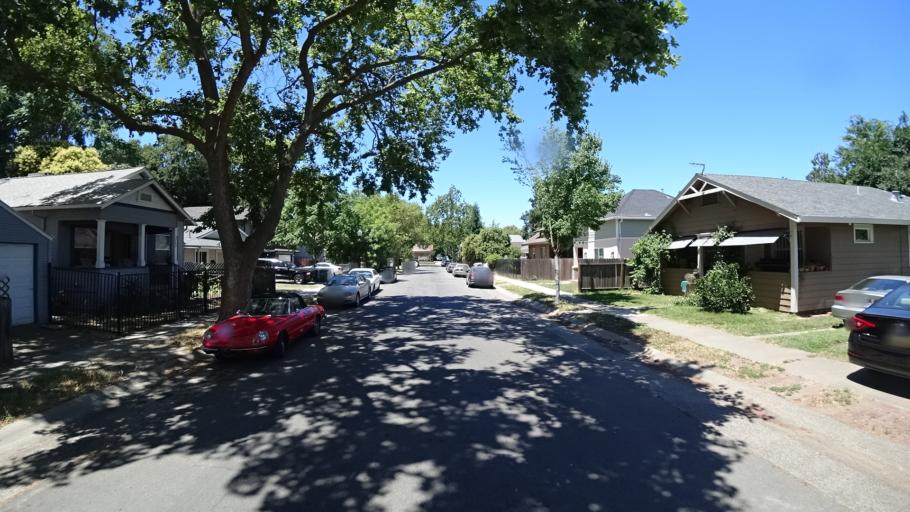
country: US
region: California
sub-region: Sacramento County
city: Sacramento
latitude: 38.5469
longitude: -121.4657
